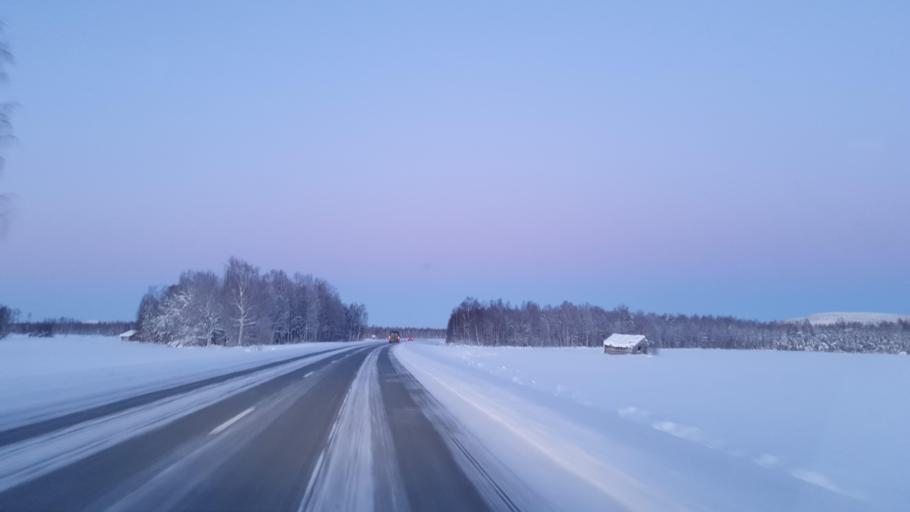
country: SE
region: Norrbotten
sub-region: Overtornea Kommun
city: OEvertornea
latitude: 66.4291
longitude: 23.6641
